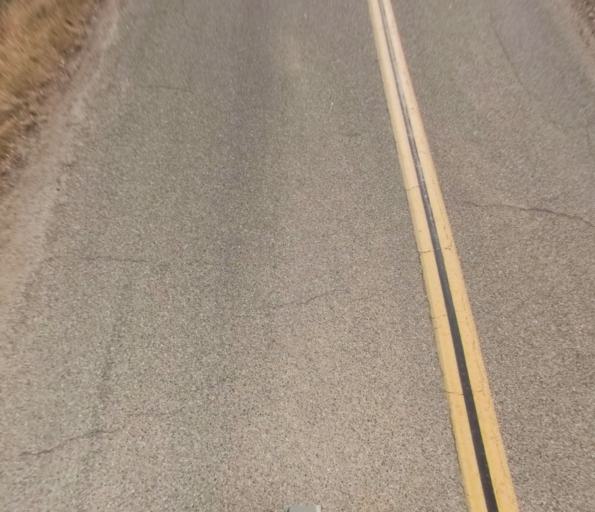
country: US
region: California
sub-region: Madera County
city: Yosemite Lakes
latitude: 37.2632
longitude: -119.9331
